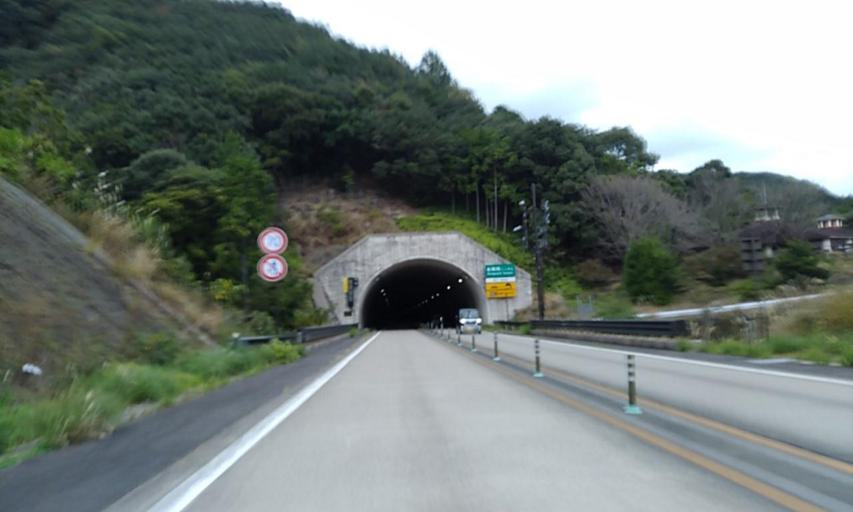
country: JP
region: Wakayama
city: Shingu
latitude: 33.6003
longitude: 135.9160
